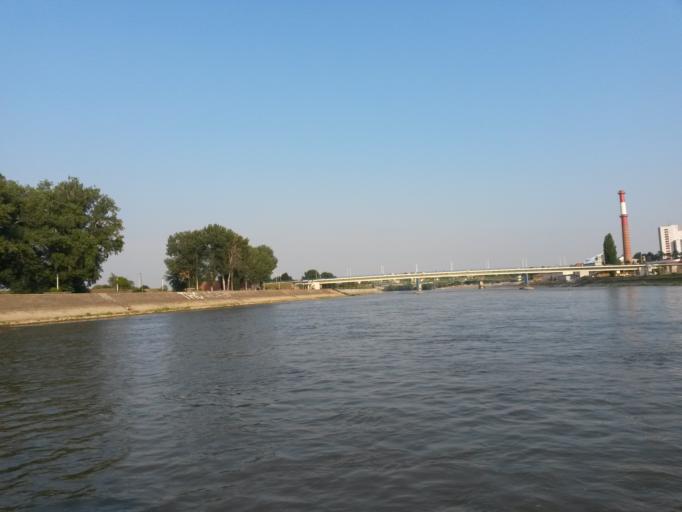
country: HR
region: Osjecko-Baranjska
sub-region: Grad Osijek
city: Osijek
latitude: 45.5640
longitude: 18.6974
